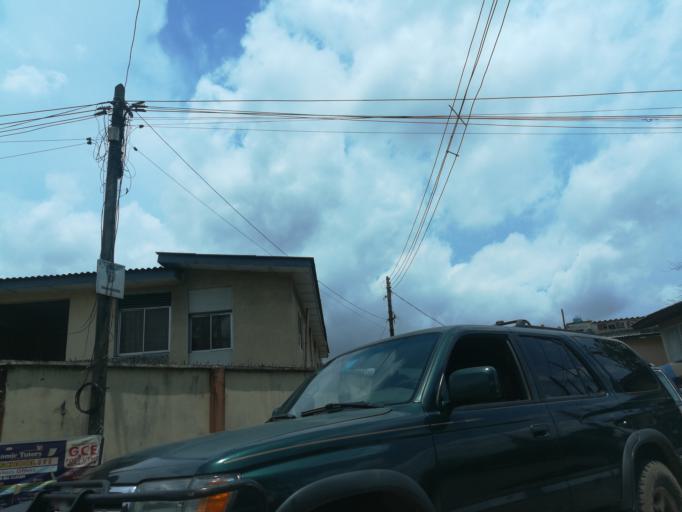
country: NG
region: Lagos
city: Somolu
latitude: 6.5483
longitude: 3.3617
